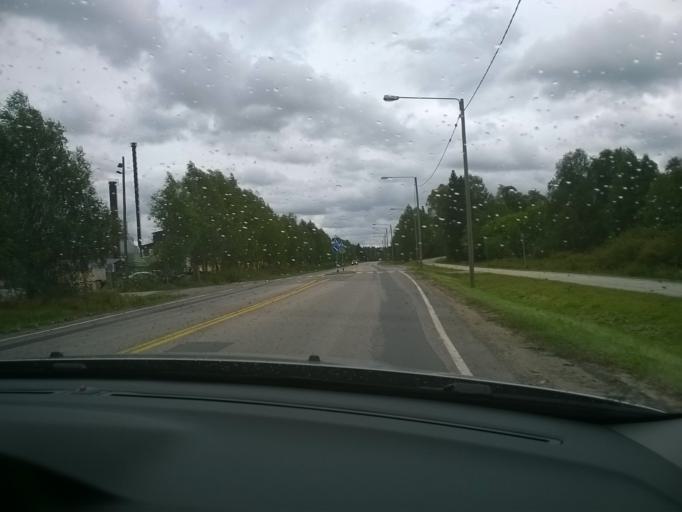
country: FI
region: Kainuu
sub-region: Kehys-Kainuu
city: Kuhmo
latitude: 64.1306
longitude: 29.4866
